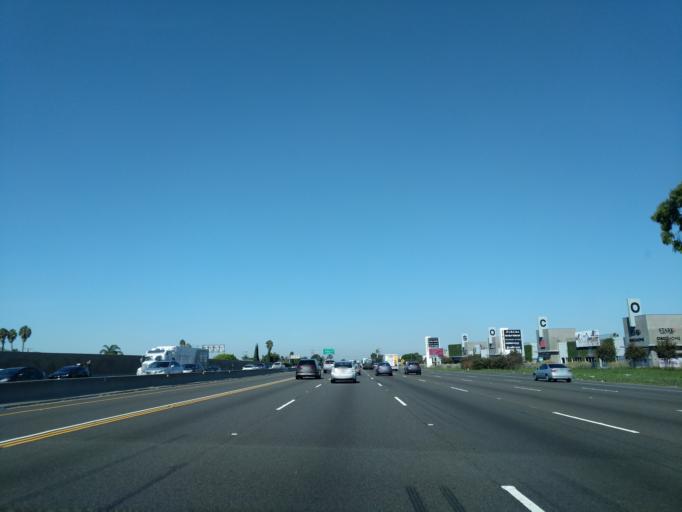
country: US
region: California
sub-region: Orange County
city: Fountain Valley
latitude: 33.6914
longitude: -117.9246
